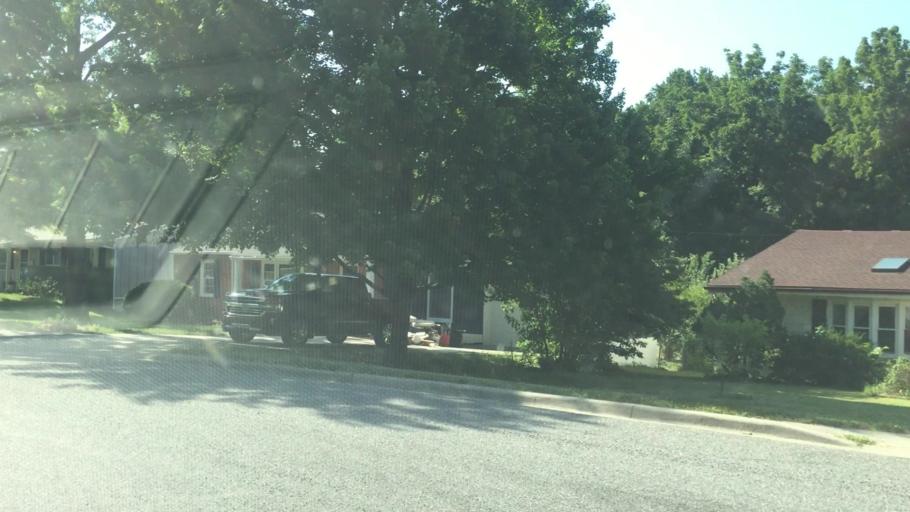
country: US
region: Kansas
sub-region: Johnson County
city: Merriam
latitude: 39.0114
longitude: -94.6769
